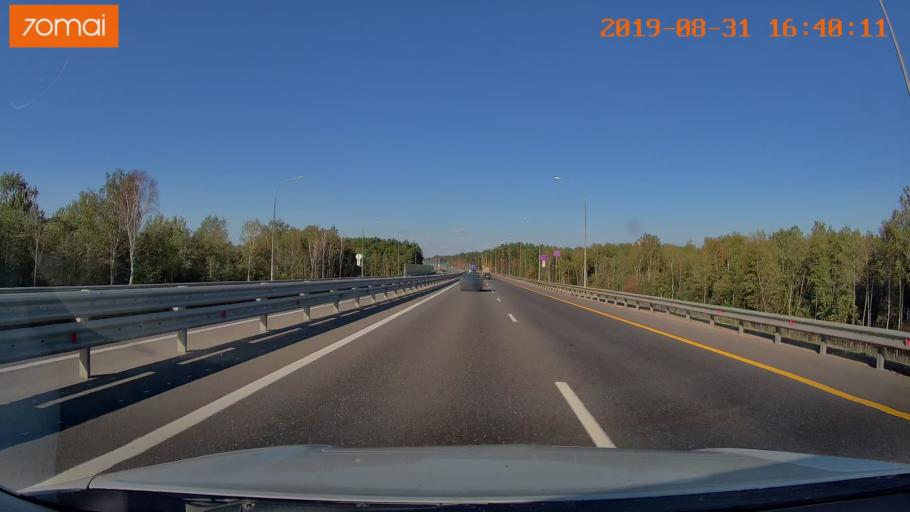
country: RU
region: Kaluga
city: Kurovskoye
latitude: 54.5618
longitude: 36.0433
